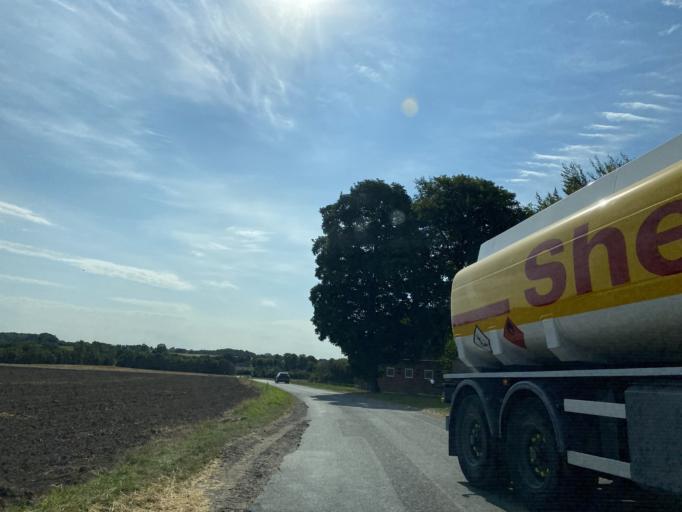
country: DK
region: Central Jutland
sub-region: Favrskov Kommune
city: Ulstrup
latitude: 56.3243
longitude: 9.7647
